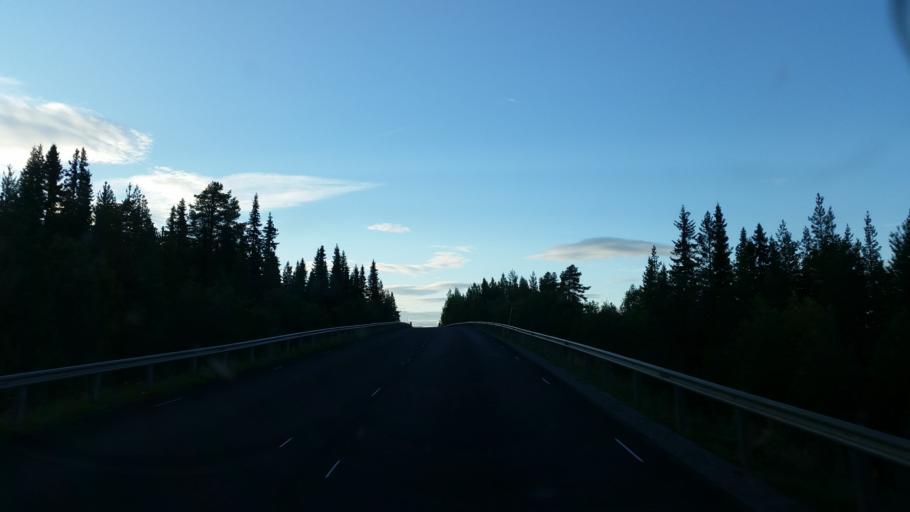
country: SE
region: Vaesterbotten
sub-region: Vilhelmina Kommun
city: Vilhelmina
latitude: 64.7395
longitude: 16.7094
